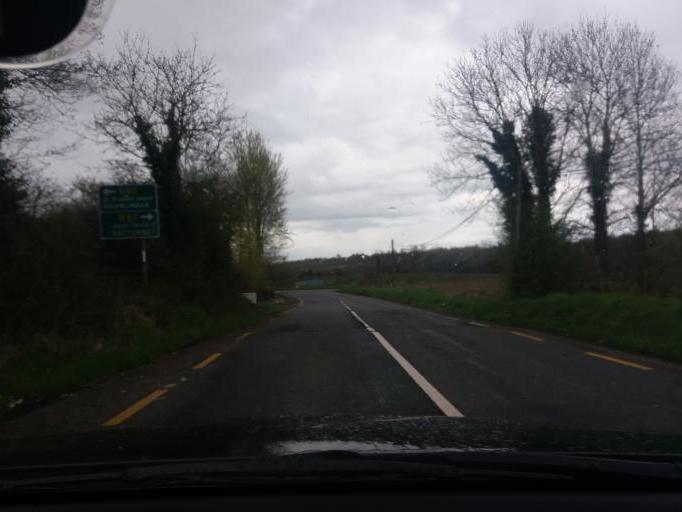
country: IE
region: Ulster
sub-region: An Cabhan
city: Ballyconnell
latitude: 54.1533
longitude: -7.7185
